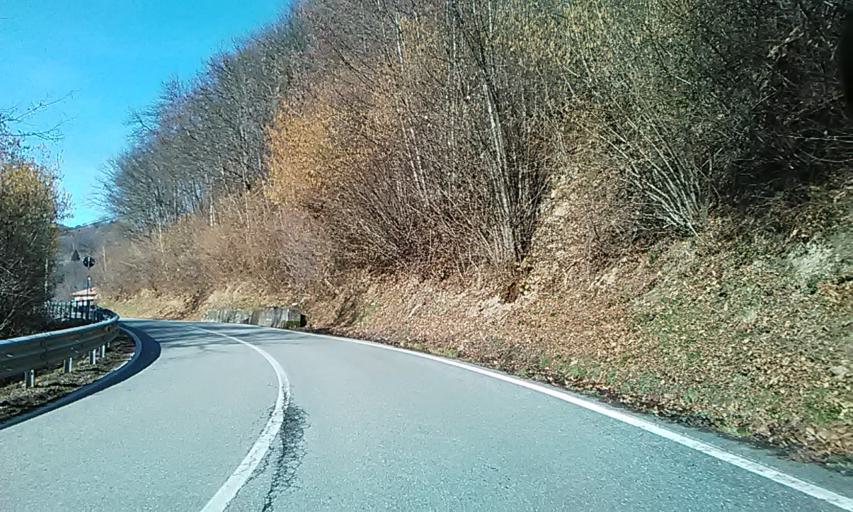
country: IT
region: Piedmont
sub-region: Provincia di Vercelli
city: Cellio
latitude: 45.7499
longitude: 8.3125
